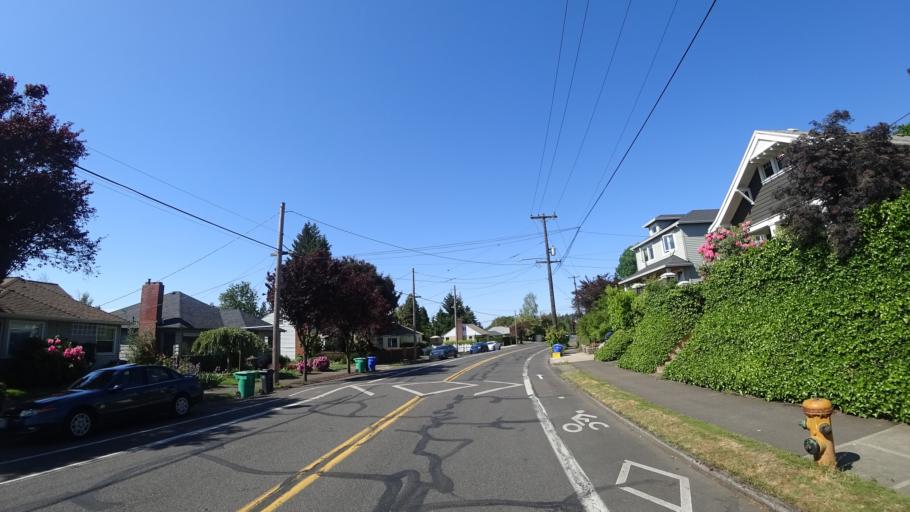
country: US
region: Oregon
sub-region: Clackamas County
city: Milwaukie
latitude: 45.4875
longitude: -122.6205
